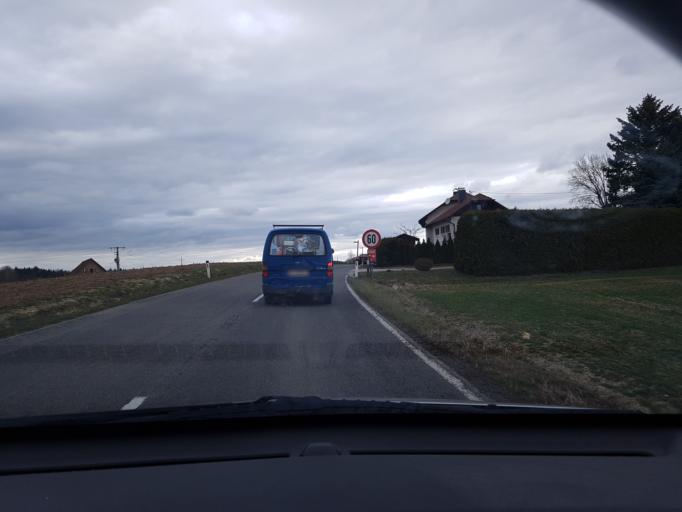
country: AT
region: Upper Austria
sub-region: Politischer Bezirk Linz-Land
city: Ansfelden
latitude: 48.1714
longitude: 14.2871
